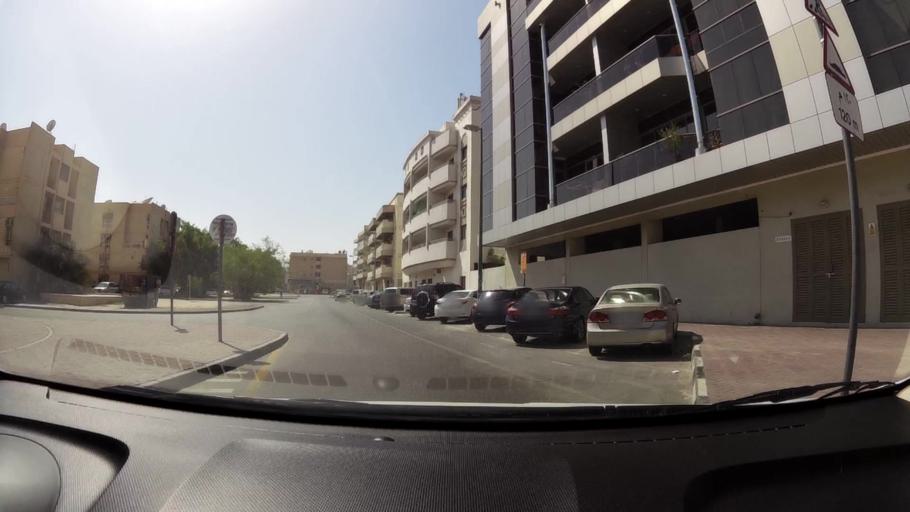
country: AE
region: Ash Shariqah
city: Sharjah
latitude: 25.2705
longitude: 55.3774
